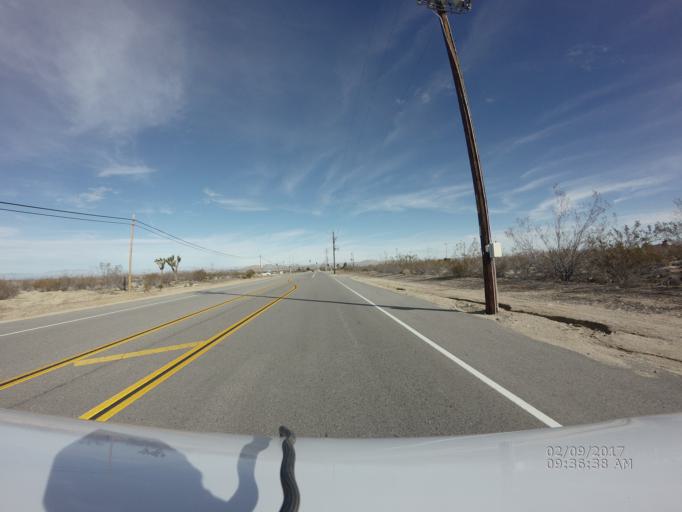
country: US
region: California
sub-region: Los Angeles County
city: Lake Los Angeles
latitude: 34.5043
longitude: -117.8354
